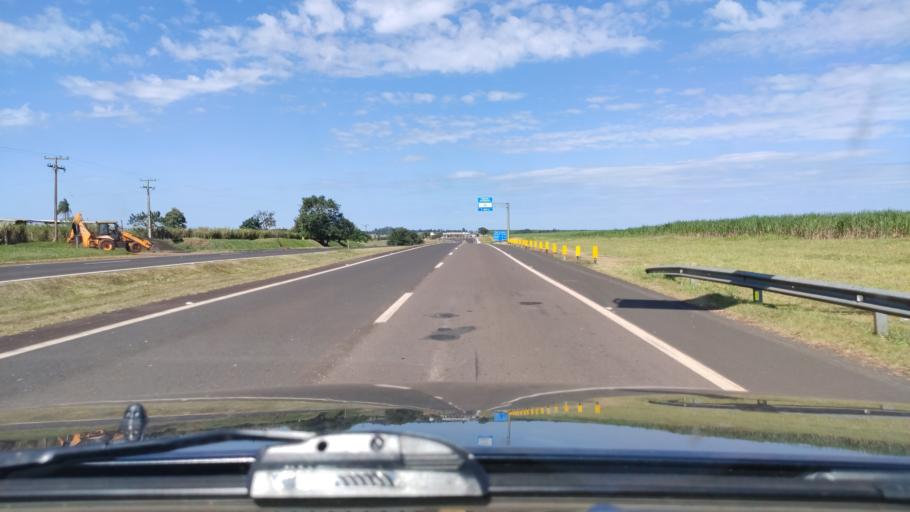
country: BR
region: Sao Paulo
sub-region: Rancharia
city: Rancharia
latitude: -22.4297
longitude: -51.0182
